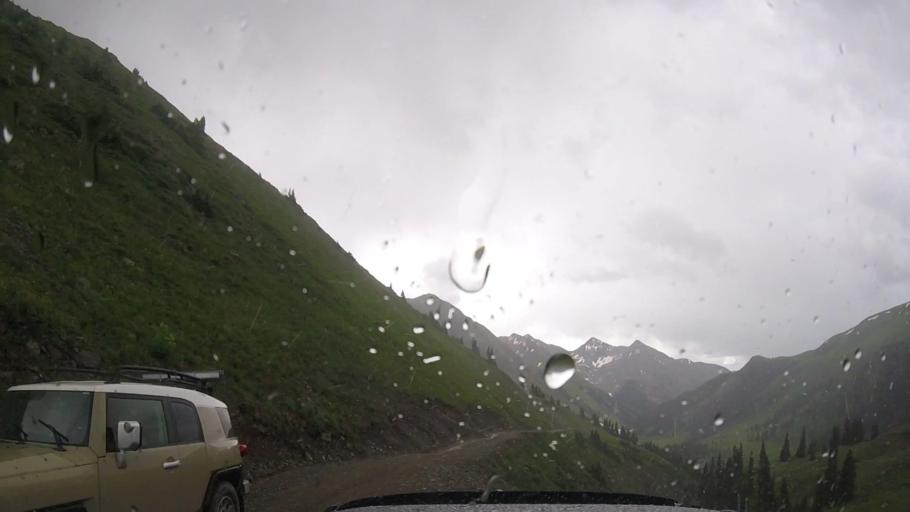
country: US
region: Colorado
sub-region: Ouray County
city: Ouray
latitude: 37.9365
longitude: -107.5710
